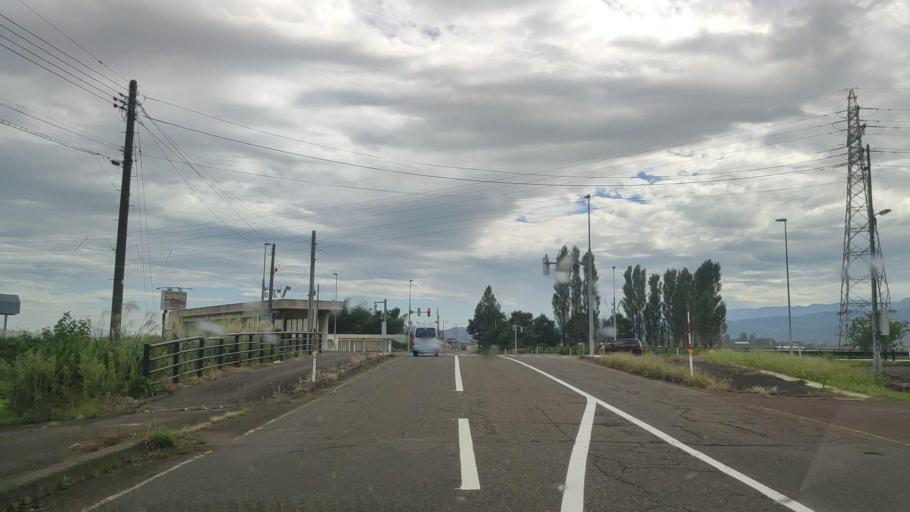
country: JP
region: Niigata
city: Joetsu
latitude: 37.0816
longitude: 138.2660
